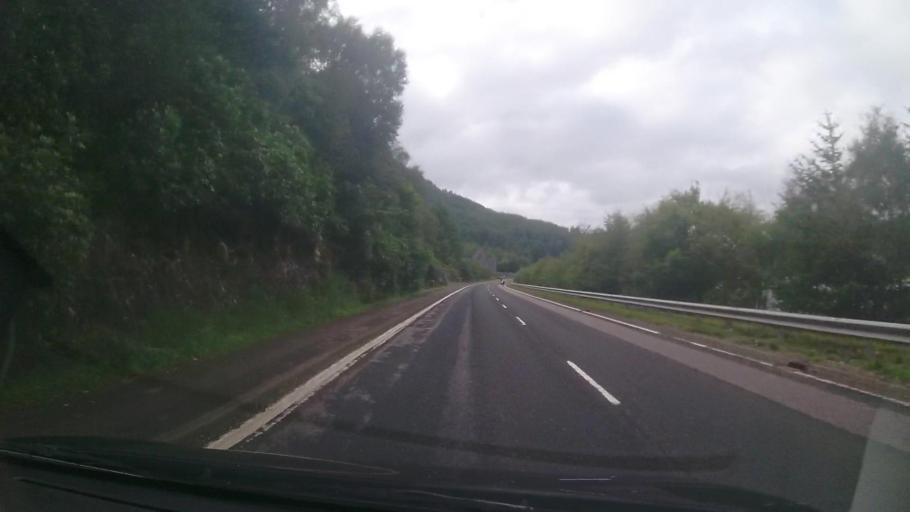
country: GB
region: Scotland
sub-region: Highland
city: Fort William
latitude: 56.6766
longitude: -5.1505
